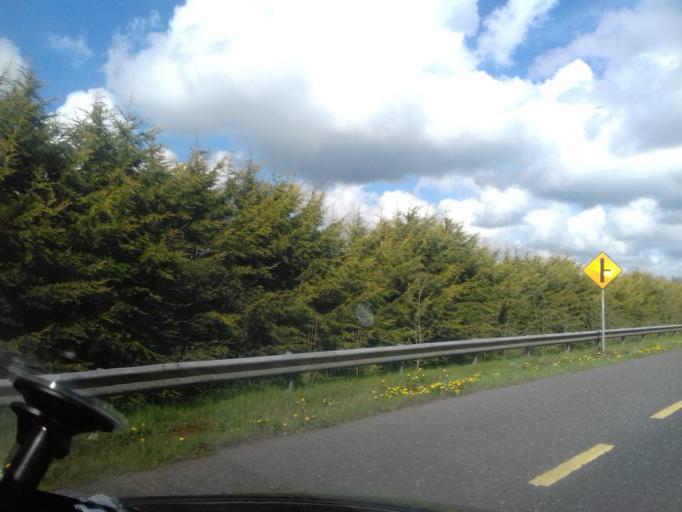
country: IE
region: Ulster
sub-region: An Cabhan
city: Virginia
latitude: 53.8609
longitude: -7.1100
